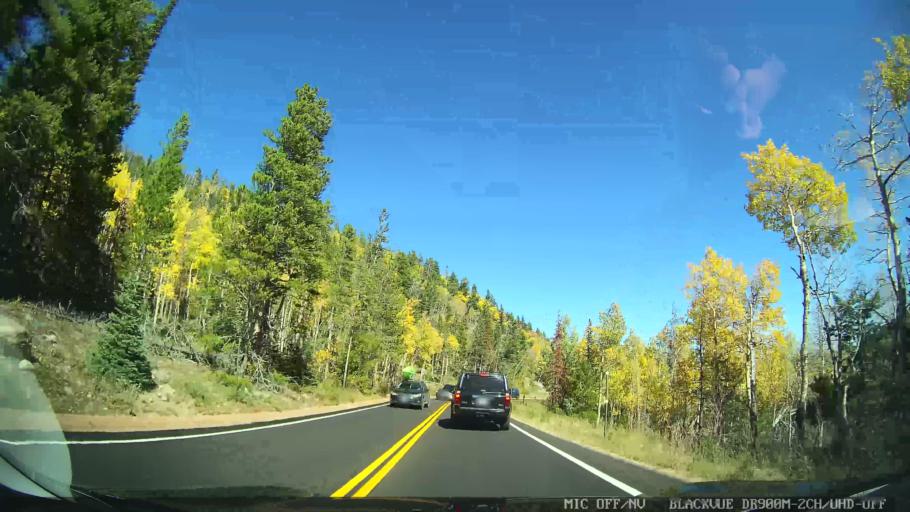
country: US
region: Colorado
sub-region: Larimer County
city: Estes Park
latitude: 40.3096
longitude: -105.6417
